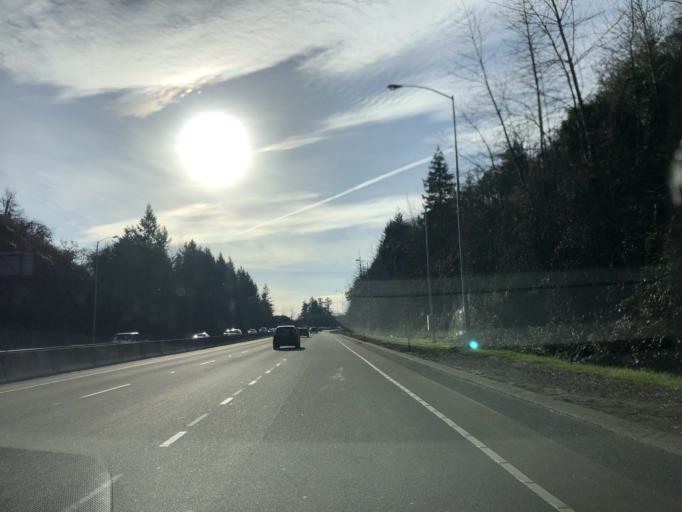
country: US
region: Oregon
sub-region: Clackamas County
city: West Linn
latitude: 45.3606
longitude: -122.6140
